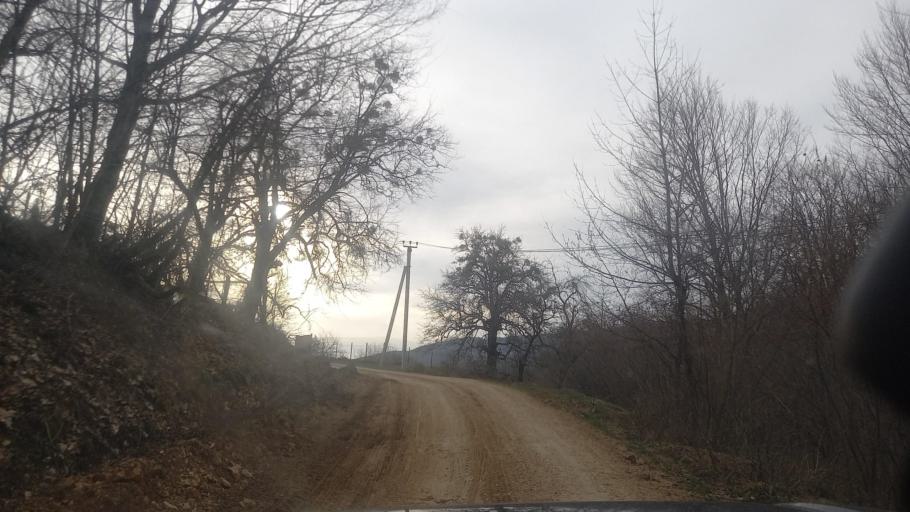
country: RU
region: Adygeya
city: Kamennomostskiy
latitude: 44.2054
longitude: 40.0070
